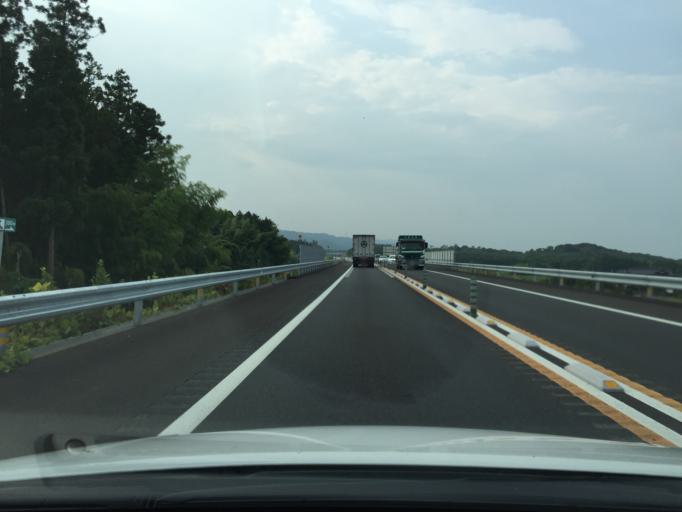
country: JP
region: Fukushima
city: Namie
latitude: 37.4841
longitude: 140.9542
